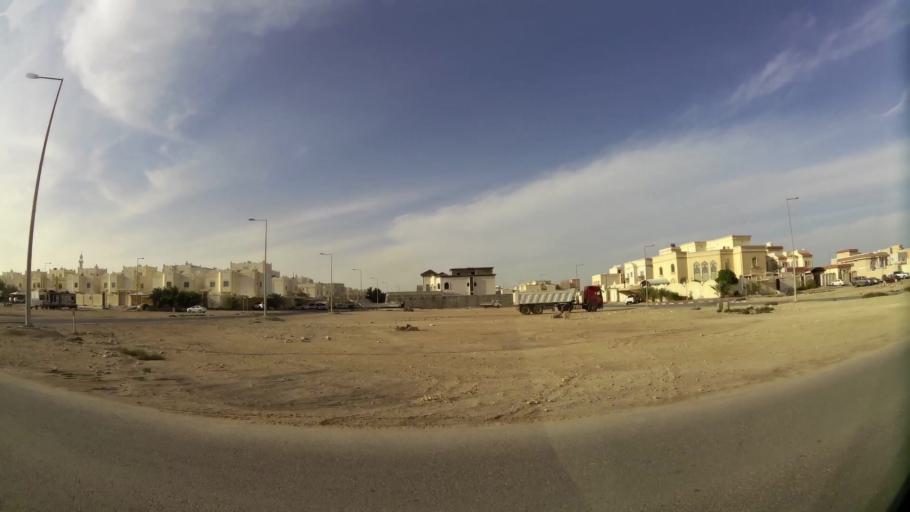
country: QA
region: Al Wakrah
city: Al Wakrah
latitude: 25.1435
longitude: 51.6118
